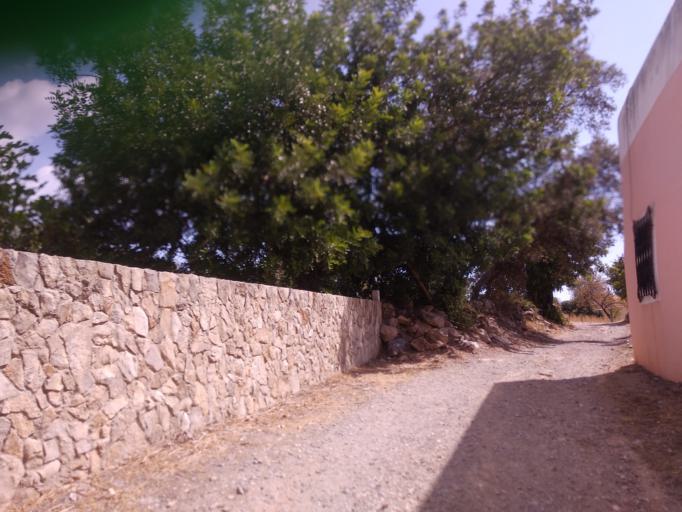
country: PT
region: Faro
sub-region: Sao Bras de Alportel
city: Sao Bras de Alportel
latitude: 37.1508
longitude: -7.8772
